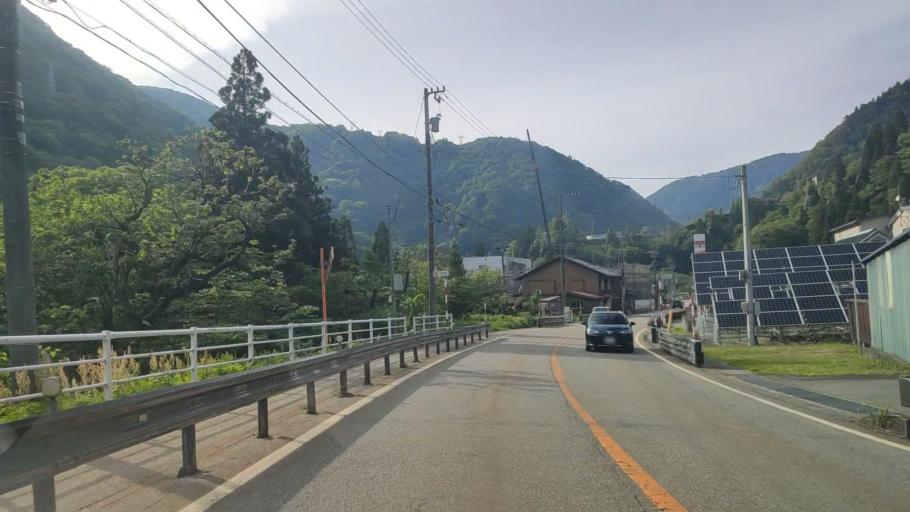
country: JP
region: Toyama
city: Yatsuomachi-higashikumisaka
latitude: 36.4333
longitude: 137.2775
